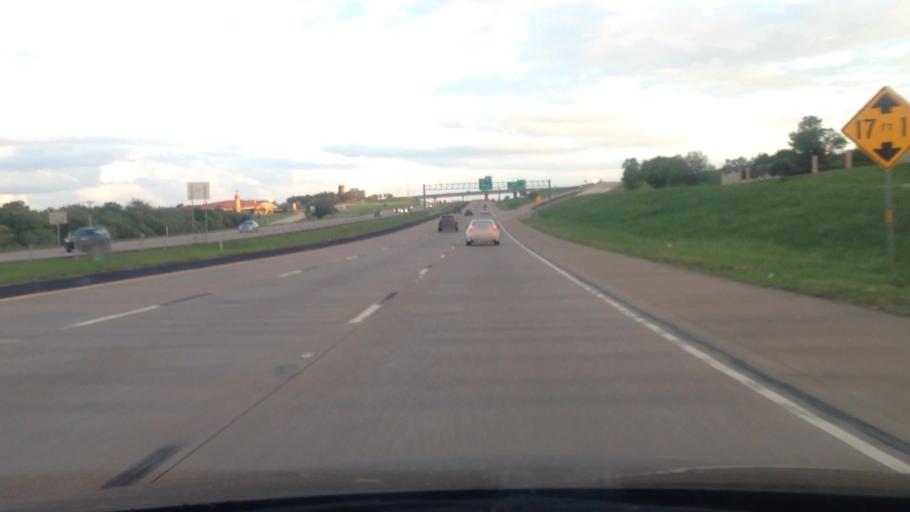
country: US
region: Texas
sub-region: Tarrant County
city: Benbrook
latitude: 32.7092
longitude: -97.4761
